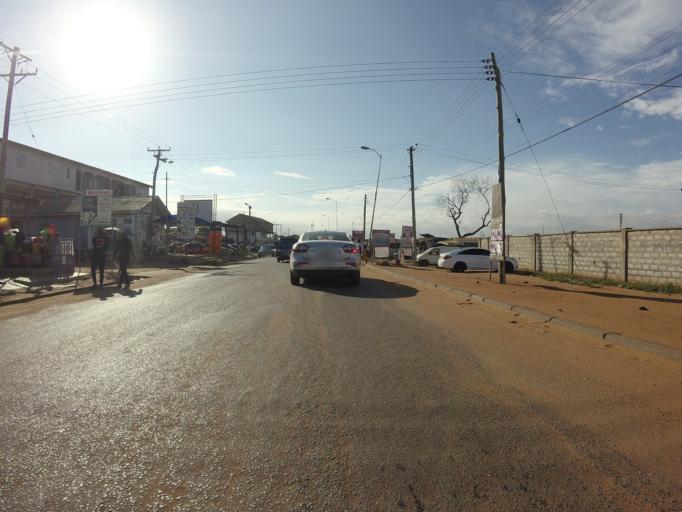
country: GH
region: Greater Accra
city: Nungua
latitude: 5.6469
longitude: -0.0600
